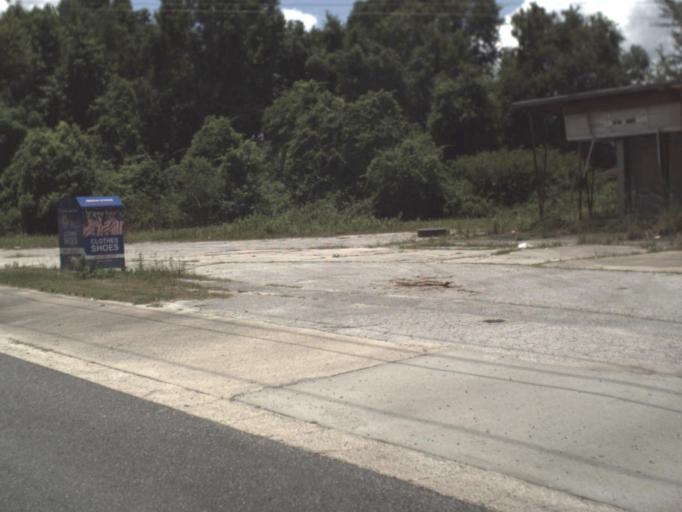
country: US
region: Florida
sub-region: Columbia County
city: Five Points
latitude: 30.2036
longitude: -82.6442
